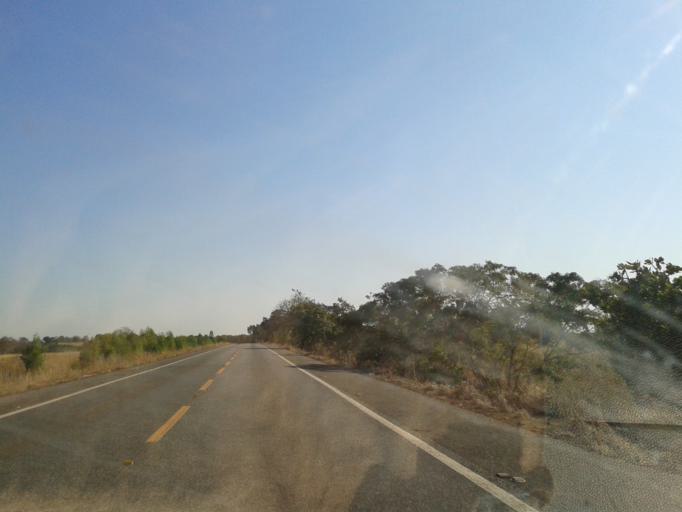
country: BR
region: Goias
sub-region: Mozarlandia
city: Mozarlandia
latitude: -14.9006
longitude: -50.5486
